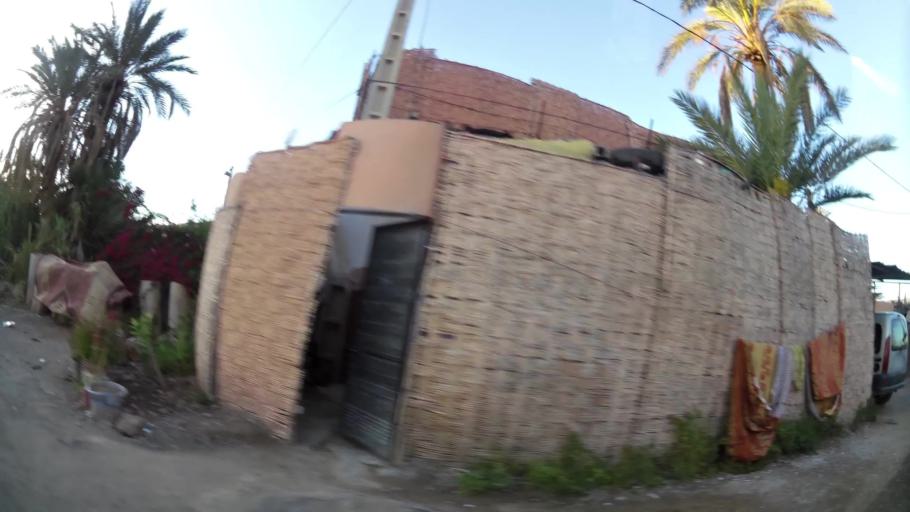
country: MA
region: Marrakech-Tensift-Al Haouz
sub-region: Marrakech
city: Marrakesh
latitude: 31.6358
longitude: -8.0341
